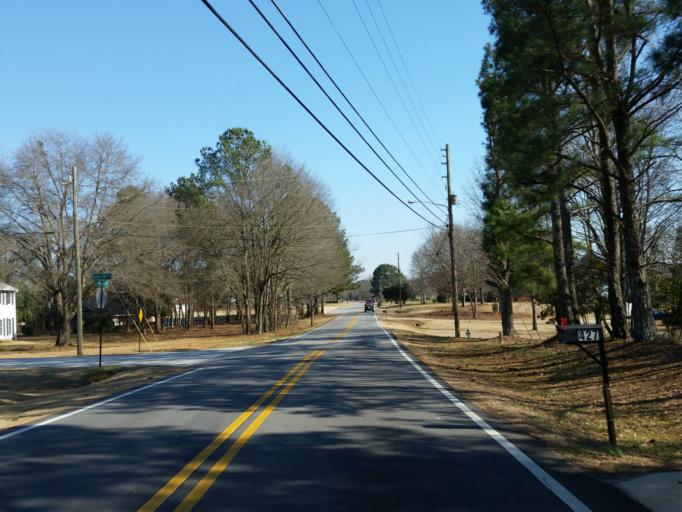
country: US
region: Georgia
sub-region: Henry County
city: Stockbridge
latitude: 33.4786
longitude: -84.2423
